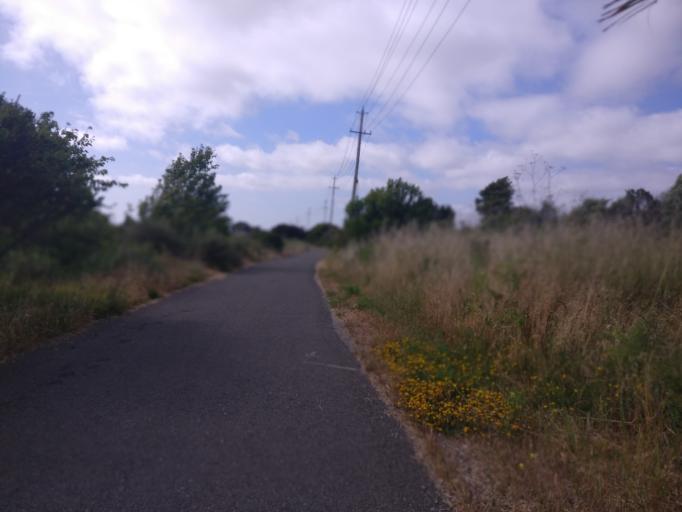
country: US
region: California
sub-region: Alameda County
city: Alameda
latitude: 37.7538
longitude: -122.2117
